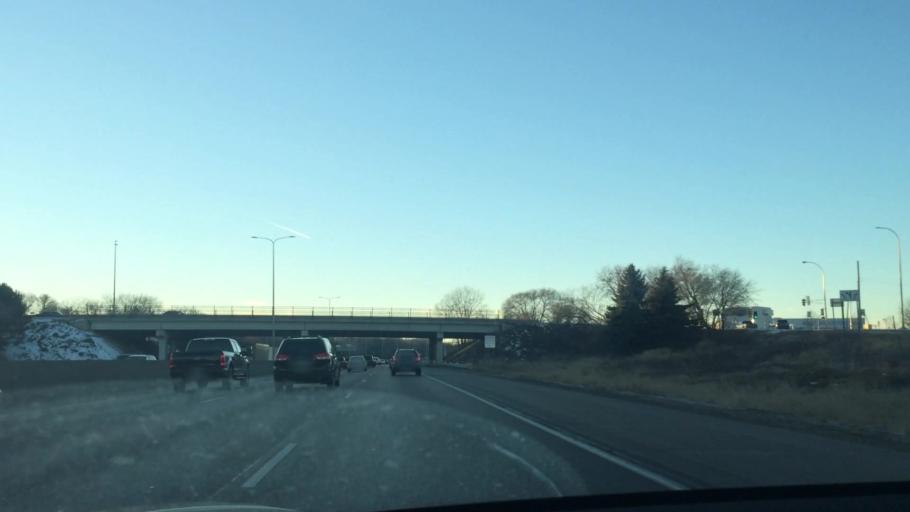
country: US
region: Minnesota
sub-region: Ramsey County
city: New Brighton
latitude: 45.0649
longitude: -93.2162
